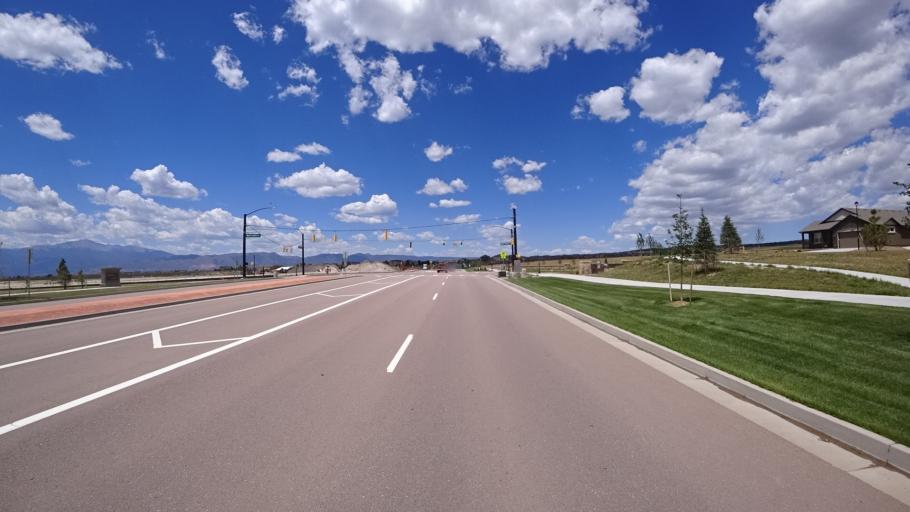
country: US
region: Colorado
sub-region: El Paso County
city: Black Forest
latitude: 38.9592
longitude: -104.7071
